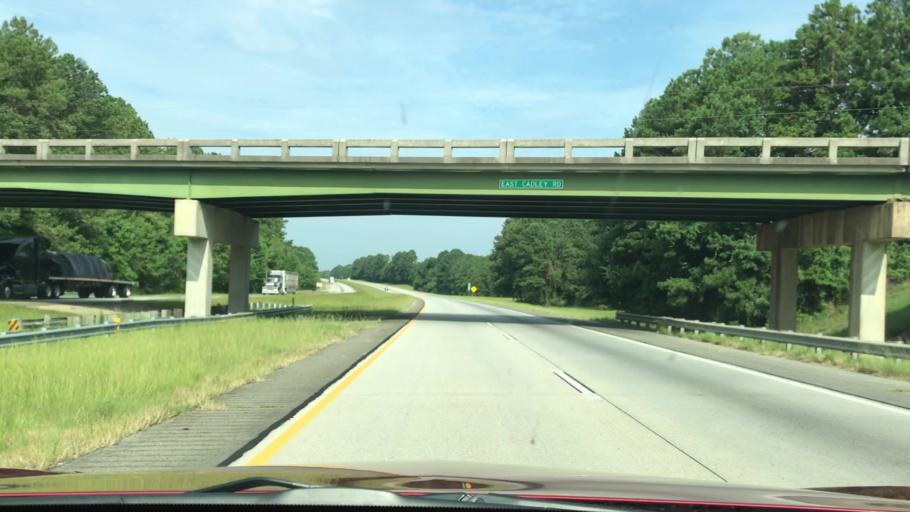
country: US
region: Georgia
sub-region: Warren County
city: Firing Range
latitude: 33.5025
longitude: -82.7127
